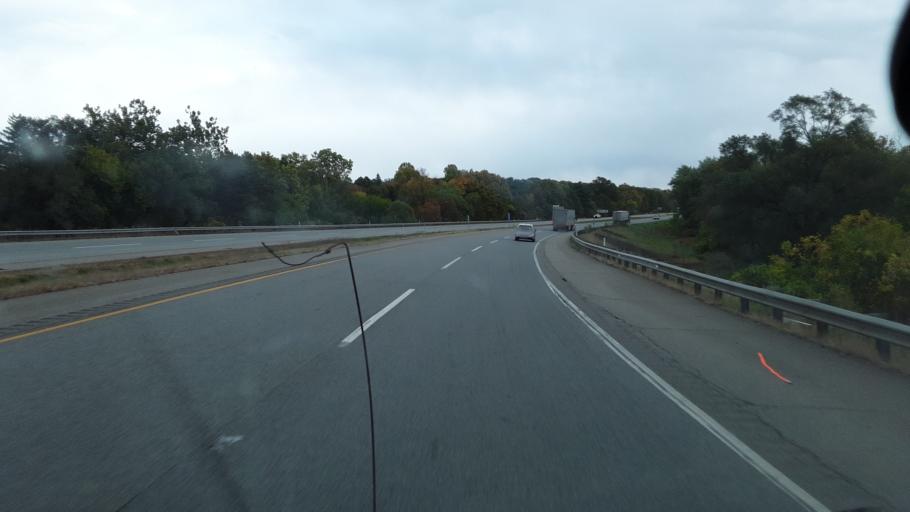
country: US
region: Indiana
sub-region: Saint Joseph County
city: Georgetown
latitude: 41.7222
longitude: -86.2490
